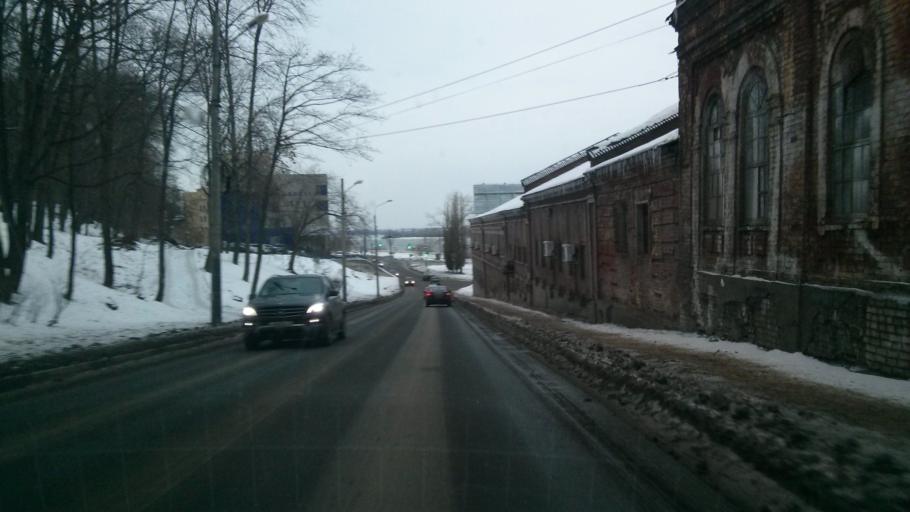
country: RU
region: Nizjnij Novgorod
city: Nizhniy Novgorod
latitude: 56.3289
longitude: 44.0268
